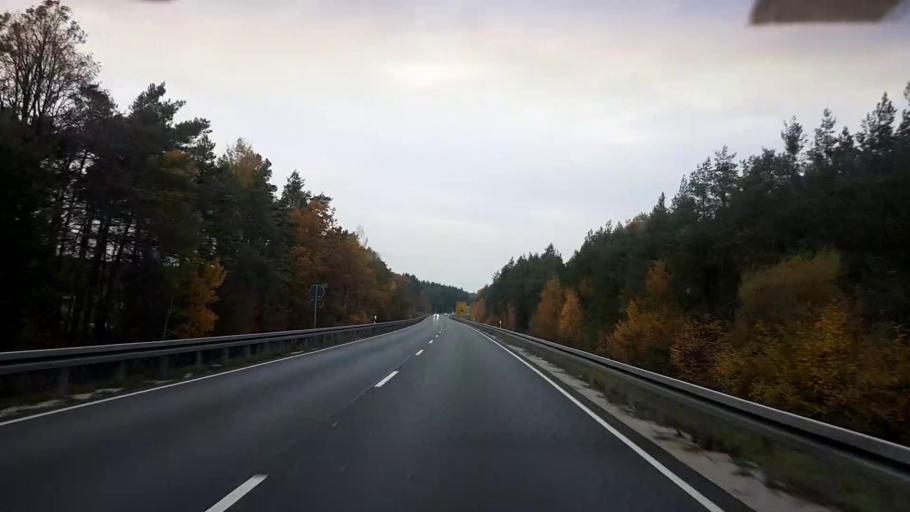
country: DE
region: Bavaria
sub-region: Regierungsbezirk Mittelfranken
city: Hochstadt an der Aisch
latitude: 49.7357
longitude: 10.8269
